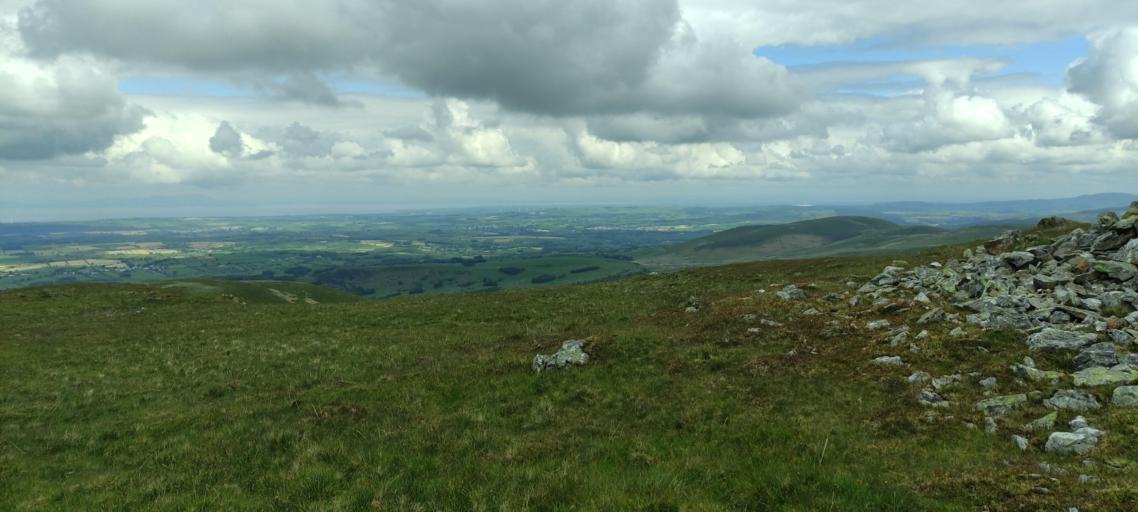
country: GB
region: England
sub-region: Cumbria
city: Cockermouth
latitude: 54.5703
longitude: -3.3672
